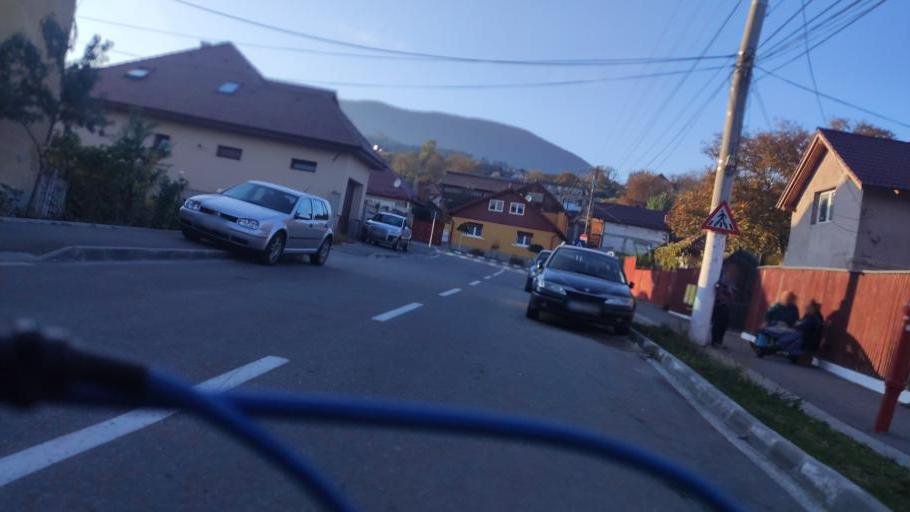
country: RO
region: Brasov
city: Codlea
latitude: 45.6921
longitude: 25.4403
